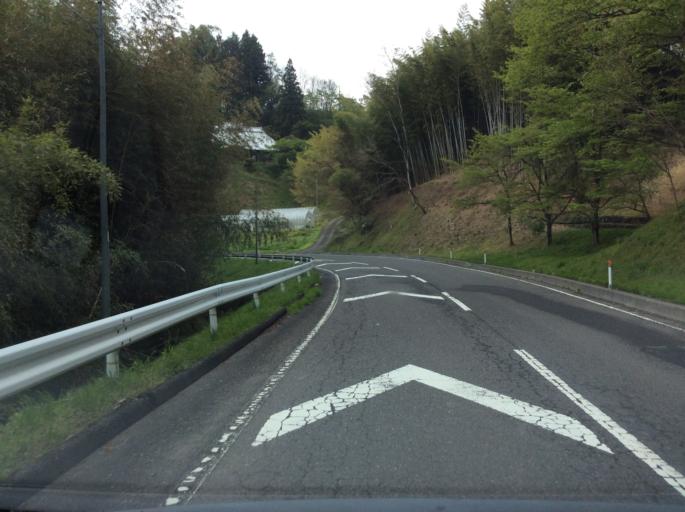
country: JP
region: Fukushima
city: Miharu
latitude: 37.3973
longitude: 140.5060
